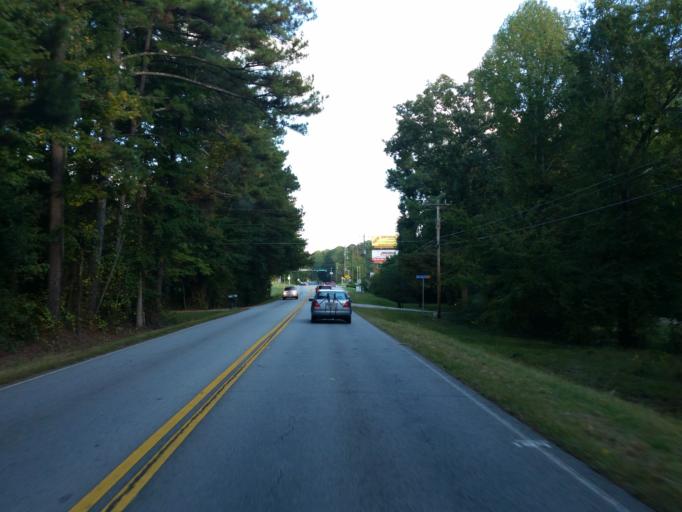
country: US
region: Georgia
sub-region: Paulding County
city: Hiram
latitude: 33.9044
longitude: -84.7292
